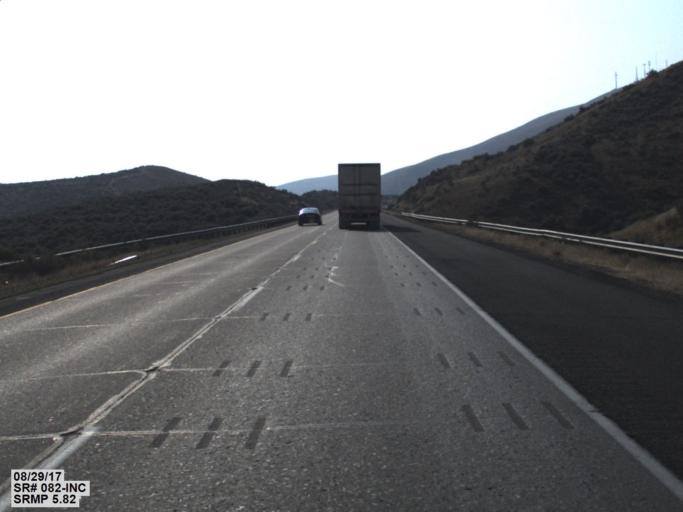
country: US
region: Washington
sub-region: Kittitas County
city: Kittitas
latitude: 46.9032
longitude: -120.4568
